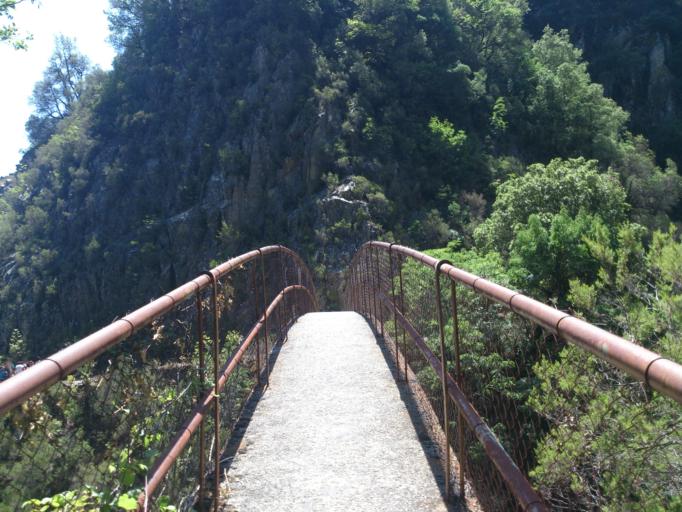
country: IT
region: Calabria
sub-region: Provincia di Reggio Calabria
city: Bivongi
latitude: 38.4980
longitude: 16.3983
